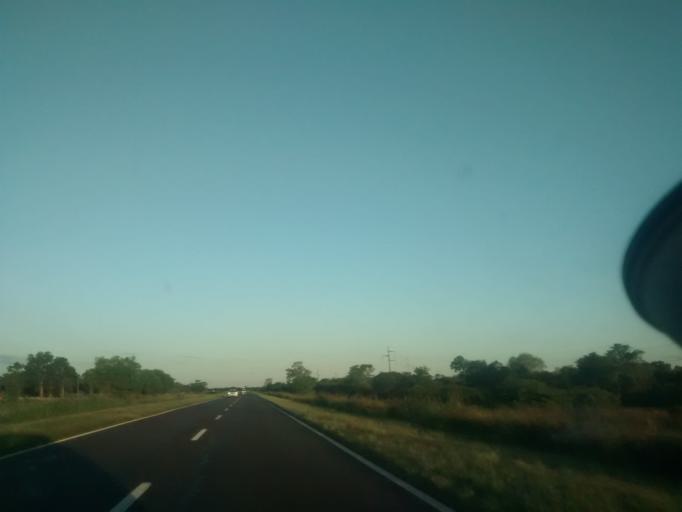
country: AR
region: Chaco
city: La Escondida
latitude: -27.1112
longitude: -59.5791
